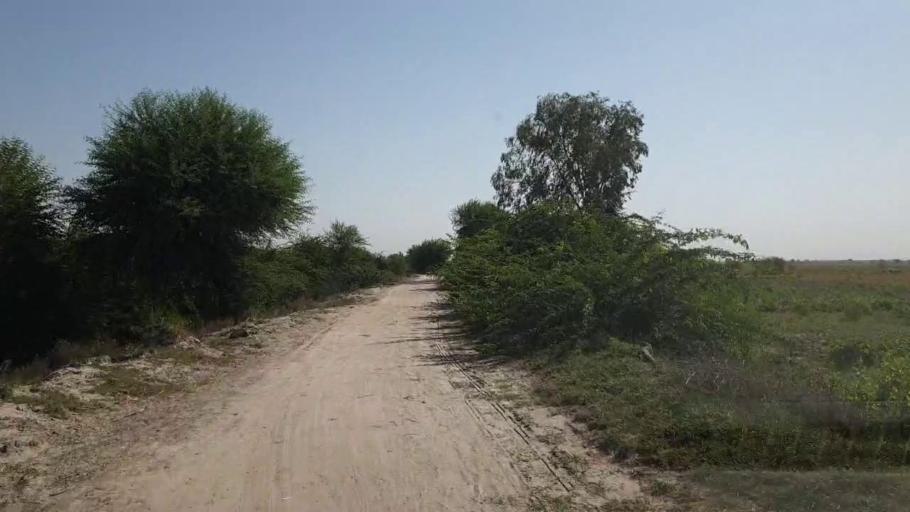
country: PK
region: Sindh
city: Kadhan
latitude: 24.6318
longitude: 68.9928
